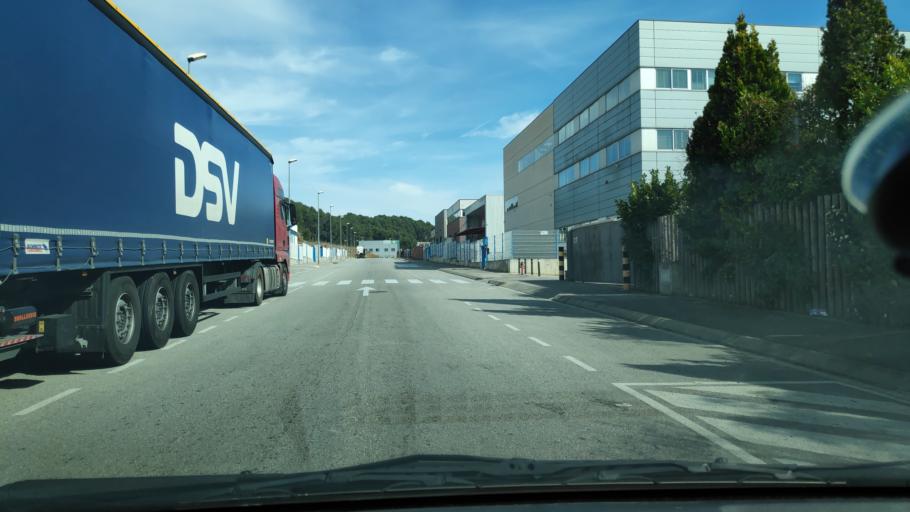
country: ES
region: Catalonia
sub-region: Provincia de Barcelona
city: Rubi
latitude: 41.5098
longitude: 2.0402
